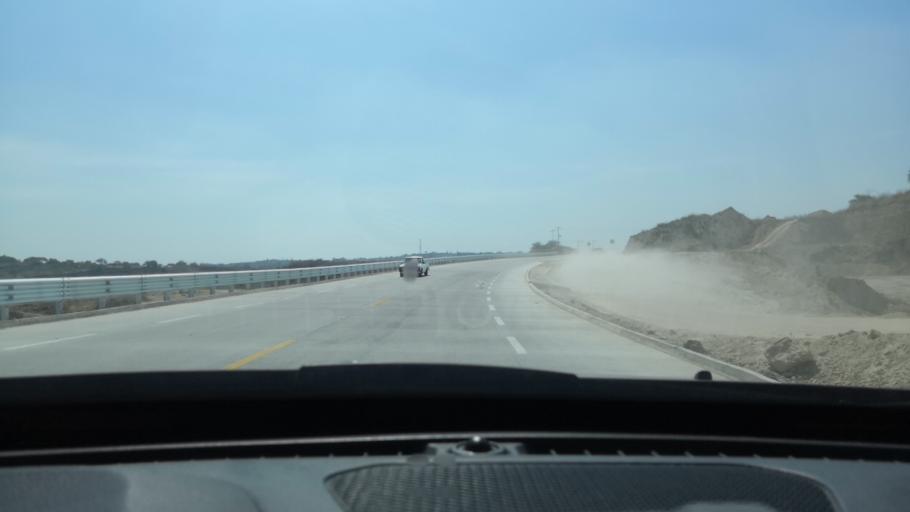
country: MX
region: Guanajuato
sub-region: Purisima del Rincon
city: Potrerillos (Guanajal)
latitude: 21.0654
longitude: -101.8718
